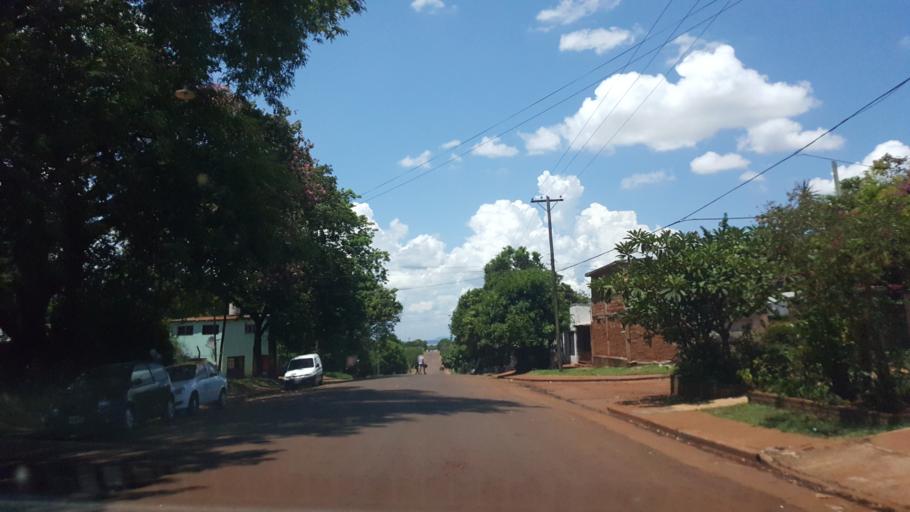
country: AR
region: Misiones
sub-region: Departamento de Capital
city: Posadas
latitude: -27.4059
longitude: -55.9218
